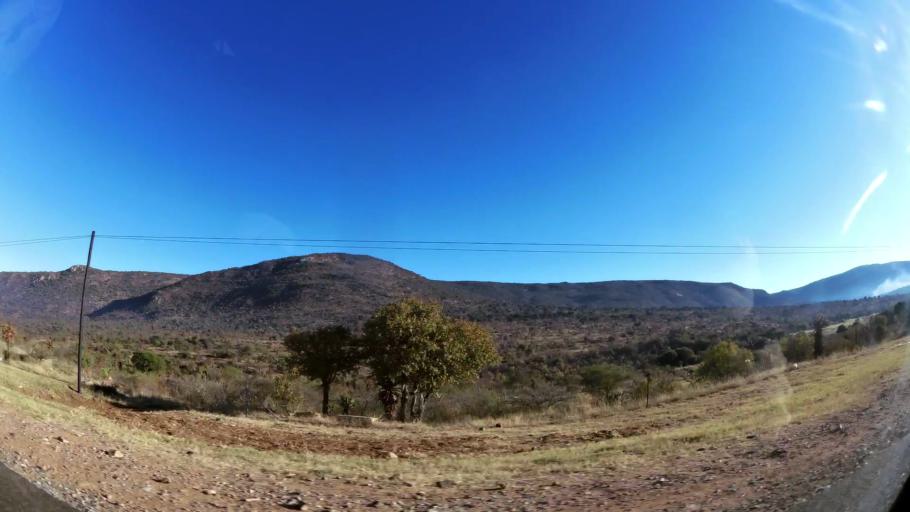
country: ZA
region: Limpopo
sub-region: Capricorn District Municipality
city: Mankoeng
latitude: -23.9414
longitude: 29.8240
